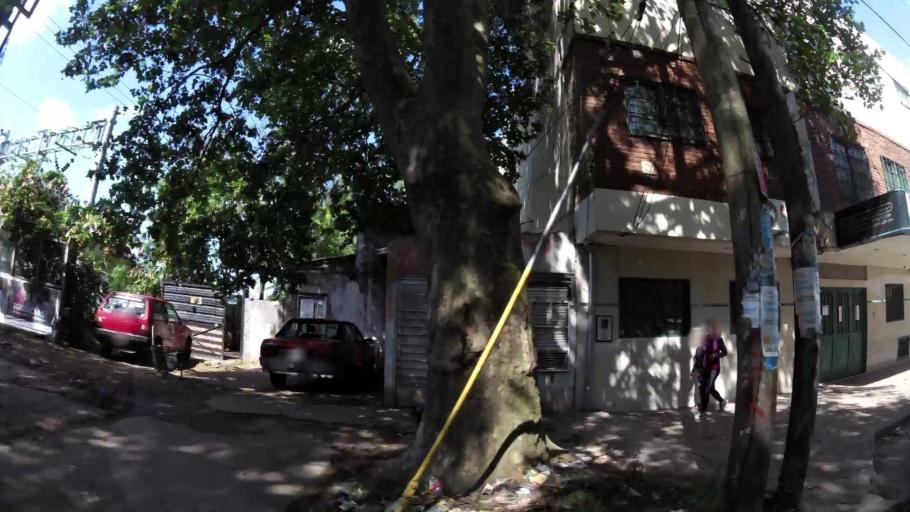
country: AR
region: Buenos Aires
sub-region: Partido de Quilmes
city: Quilmes
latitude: -34.8112
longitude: -58.2697
